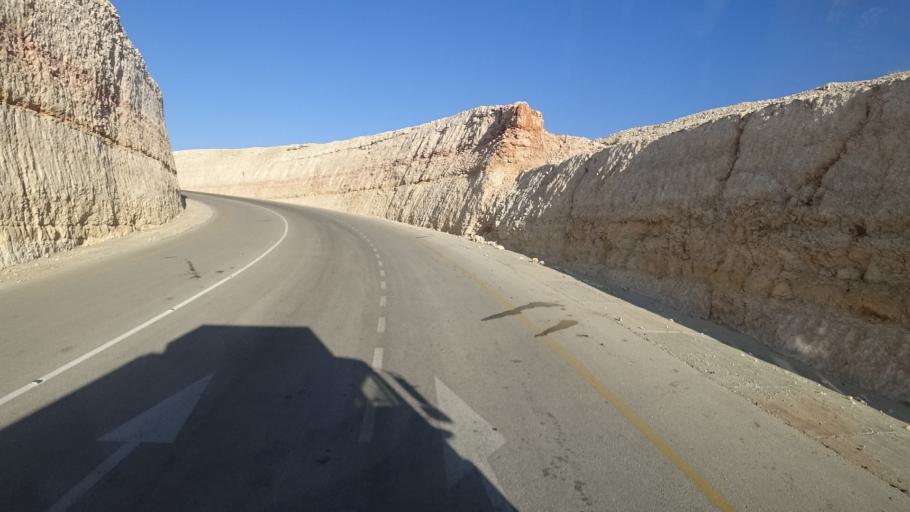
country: YE
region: Al Mahrah
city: Hawf
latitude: 17.0924
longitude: 53.0628
